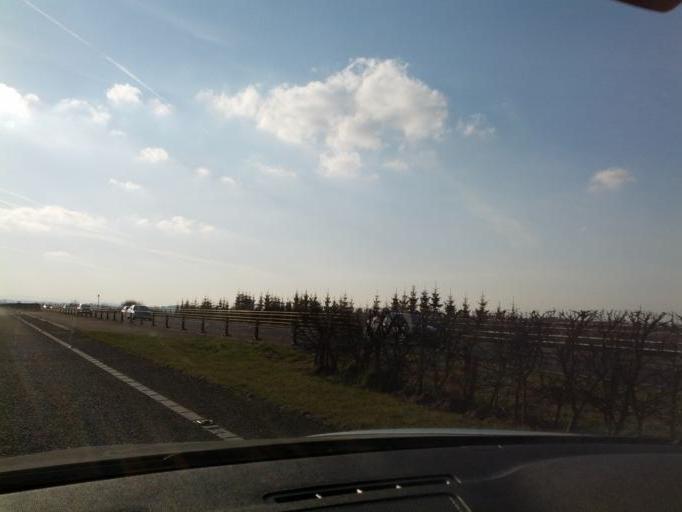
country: IE
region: Leinster
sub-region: Kildare
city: Cherryville
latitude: 53.1511
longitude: -6.9788
